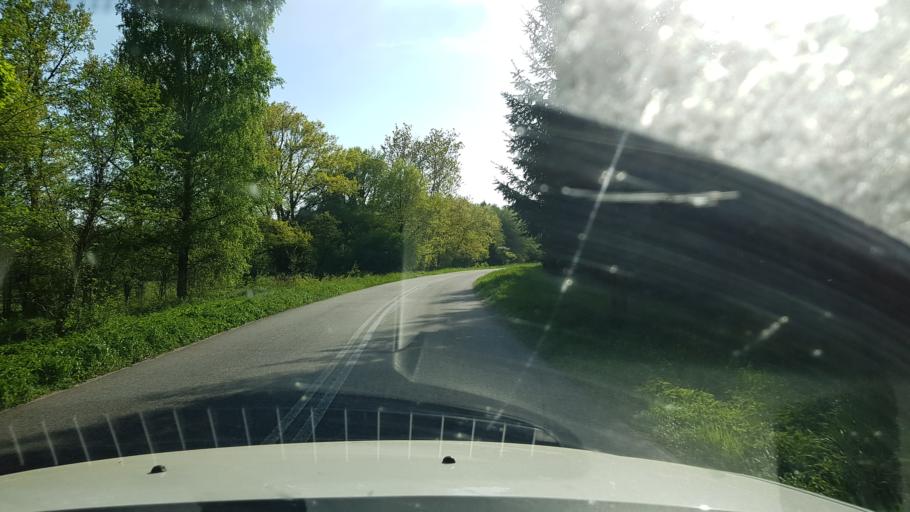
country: PL
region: West Pomeranian Voivodeship
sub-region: Powiat lobeski
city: Resko
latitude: 53.7342
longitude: 15.3538
